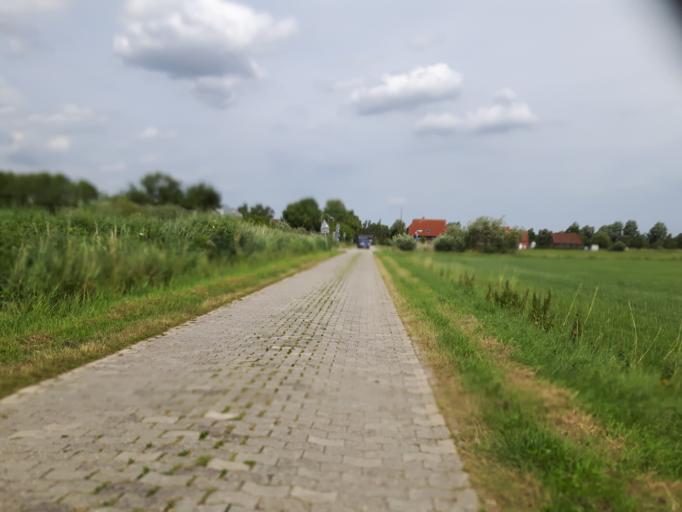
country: DE
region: Lower Saxony
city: Varel
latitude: 53.4055
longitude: 8.1818
